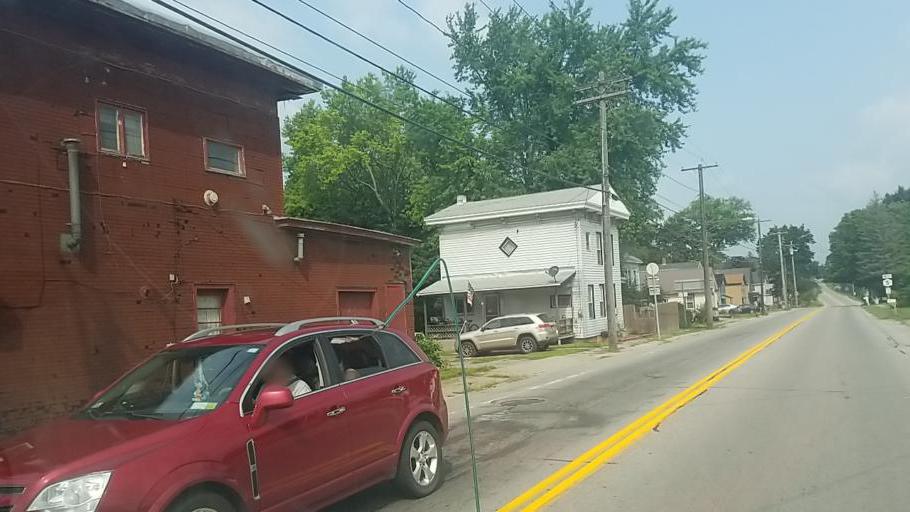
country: US
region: New York
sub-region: Montgomery County
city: Fort Plain
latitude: 42.9348
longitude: -74.6138
